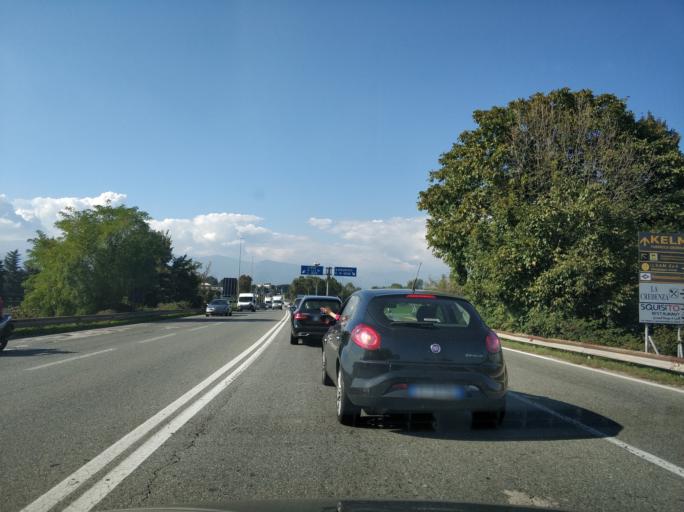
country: IT
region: Piedmont
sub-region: Provincia di Torino
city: Caselle Torinese
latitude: 45.1881
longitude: 7.6413
